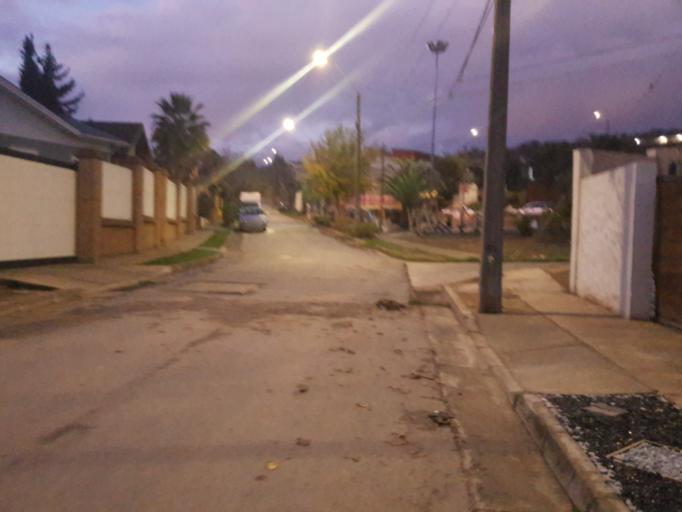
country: CL
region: Valparaiso
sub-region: Provincia de Marga Marga
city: Villa Alemana
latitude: -33.0378
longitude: -71.3488
